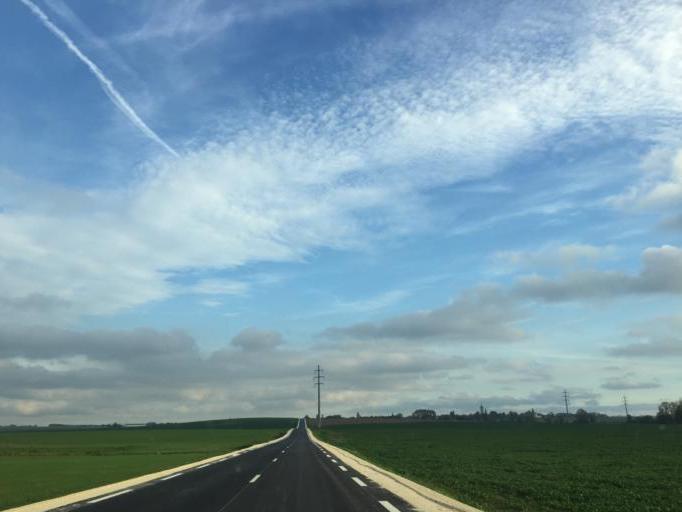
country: FR
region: Ile-de-France
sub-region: Departement de Seine-et-Marne
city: Touquin
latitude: 48.7014
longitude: 3.0640
